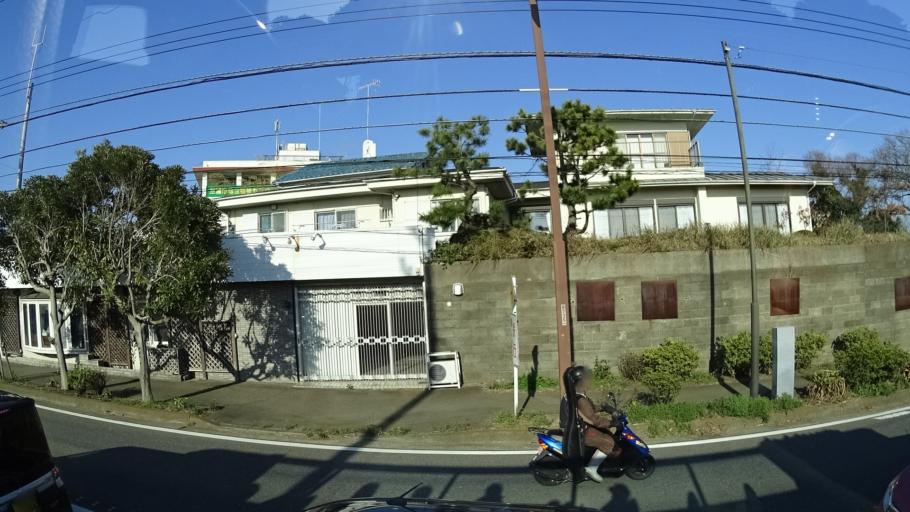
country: JP
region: Kanagawa
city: Miura
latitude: 35.1658
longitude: 139.6429
